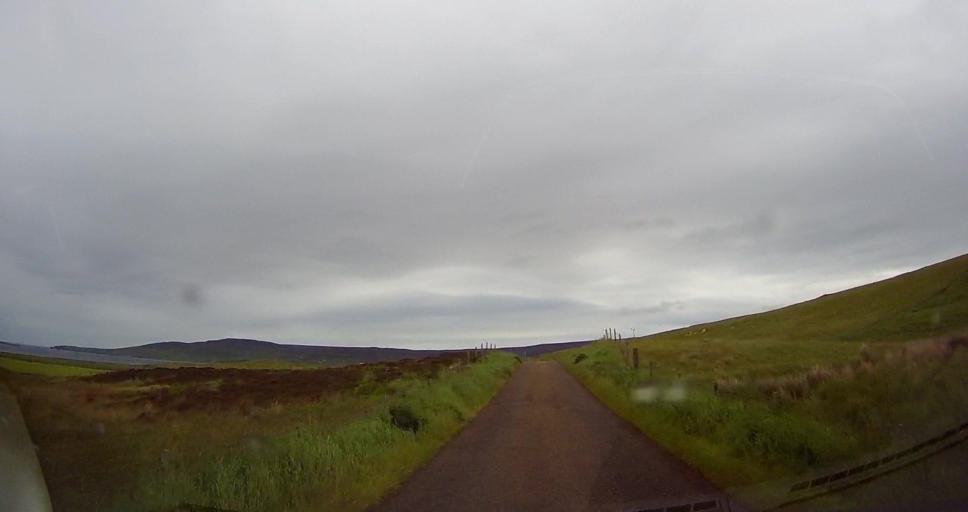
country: GB
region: Scotland
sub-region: Orkney Islands
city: Orkney
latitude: 59.1071
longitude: -3.0834
